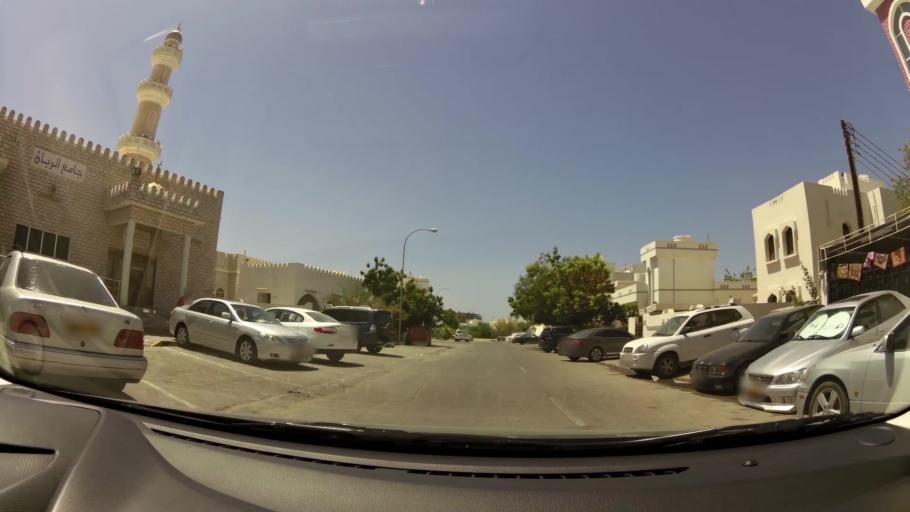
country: OM
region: Muhafazat Masqat
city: Bawshar
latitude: 23.5957
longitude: 58.3726
